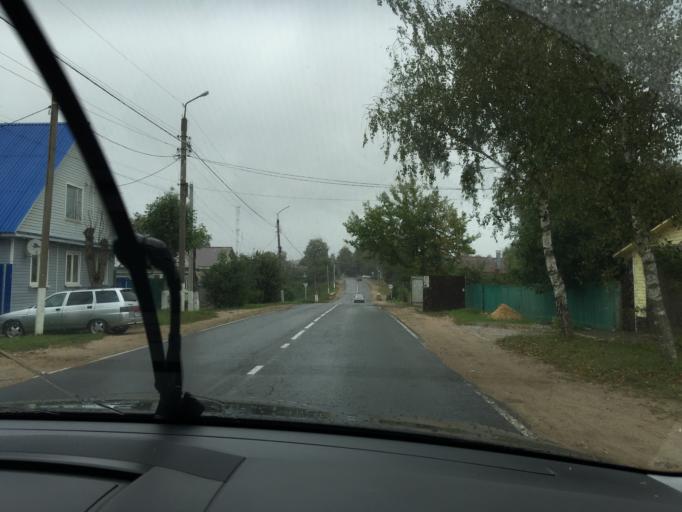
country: RU
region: Kaluga
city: Borovsk
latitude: 55.1958
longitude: 36.4795
